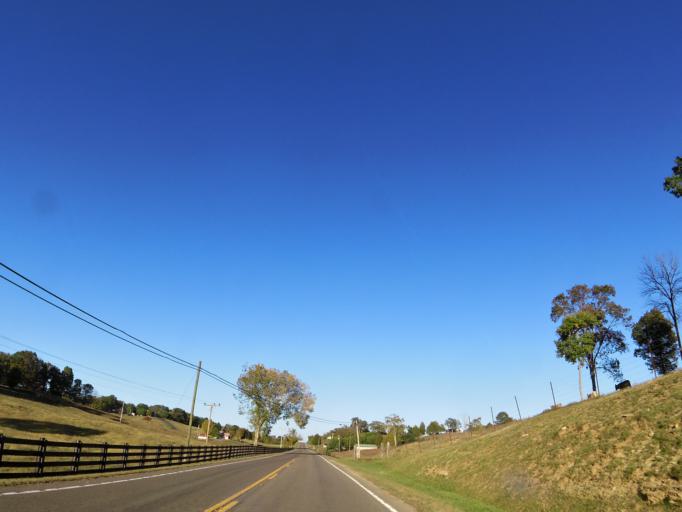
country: US
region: Tennessee
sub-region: Grainger County
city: Bean Station
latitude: 36.3615
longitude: -83.4119
